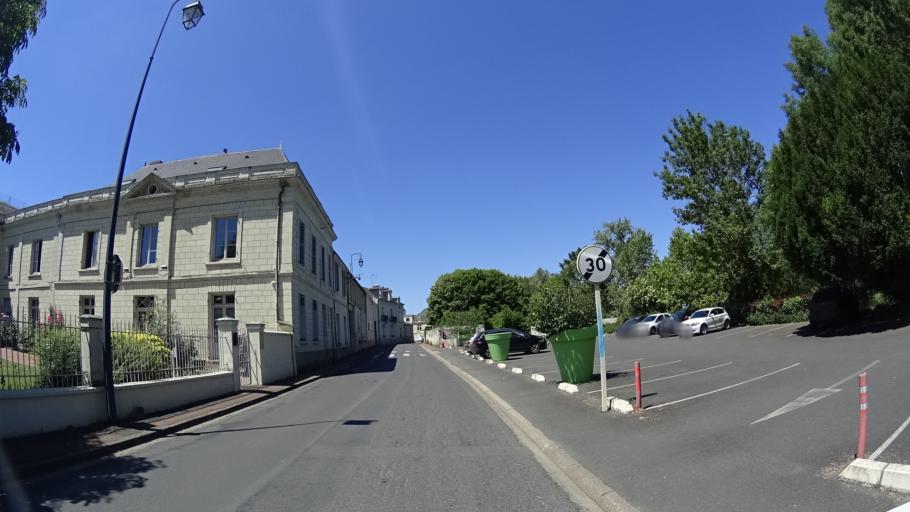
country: FR
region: Pays de la Loire
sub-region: Departement de Maine-et-Loire
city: Saumur
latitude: 47.2722
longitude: -0.1062
